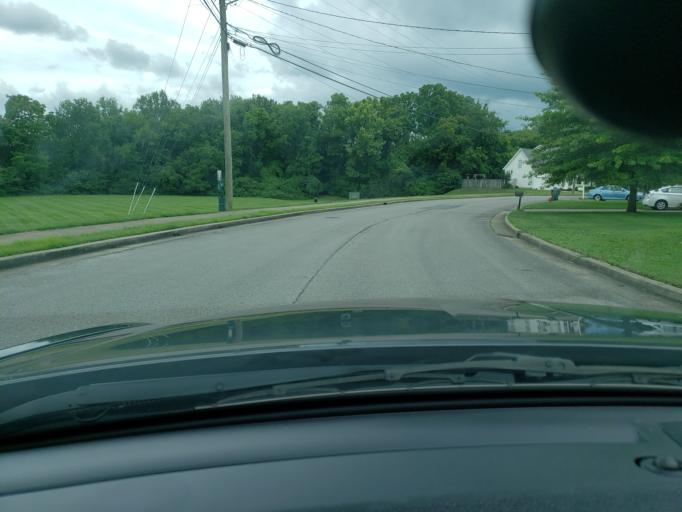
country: US
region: Tennessee
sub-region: Williamson County
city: Nolensville
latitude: 36.0214
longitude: -86.6864
